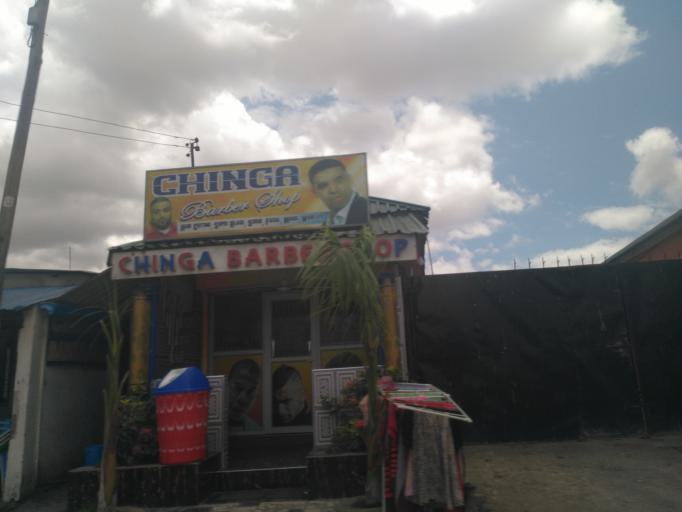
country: TZ
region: Dar es Salaam
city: Dar es Salaam
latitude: -6.8665
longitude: 39.2693
